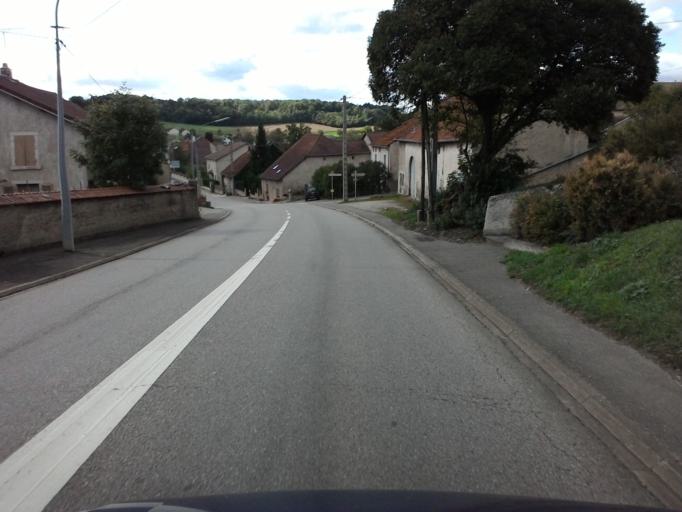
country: FR
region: Lorraine
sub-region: Departement des Vosges
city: Neufchateau
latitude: 48.4036
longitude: 5.7346
